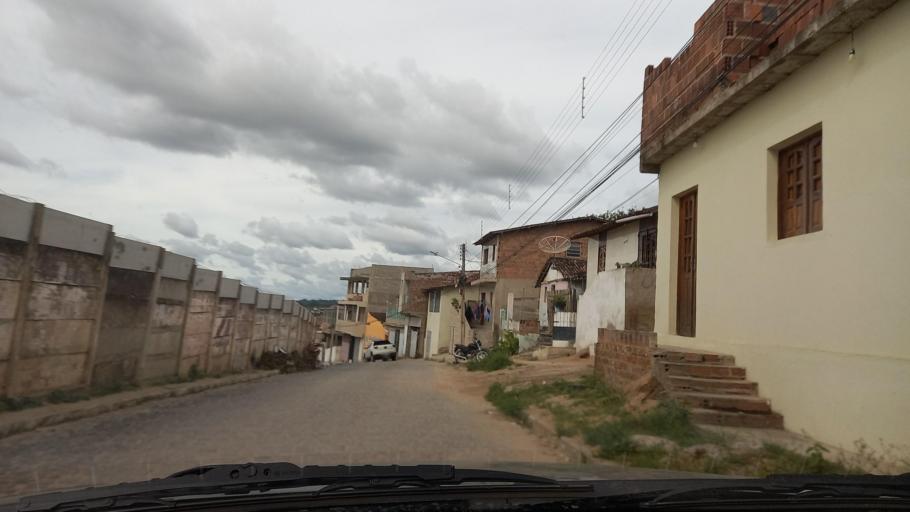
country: BR
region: Pernambuco
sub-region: Gravata
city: Gravata
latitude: -8.2091
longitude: -35.5744
